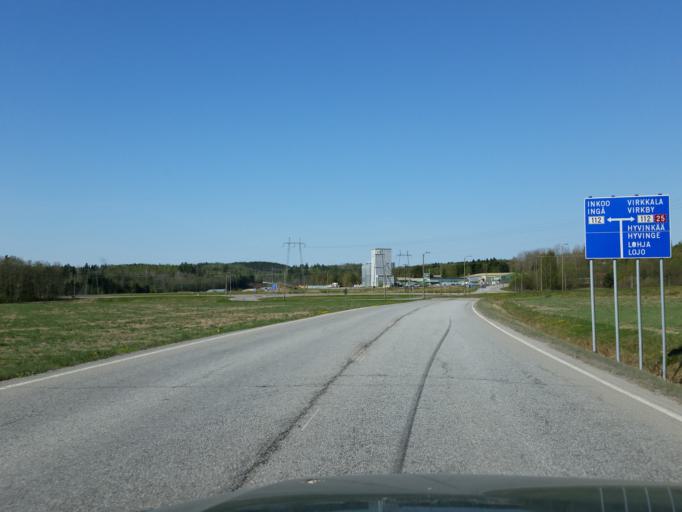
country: FI
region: Uusimaa
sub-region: Helsinki
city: Lohja
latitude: 60.1773
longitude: 23.9947
